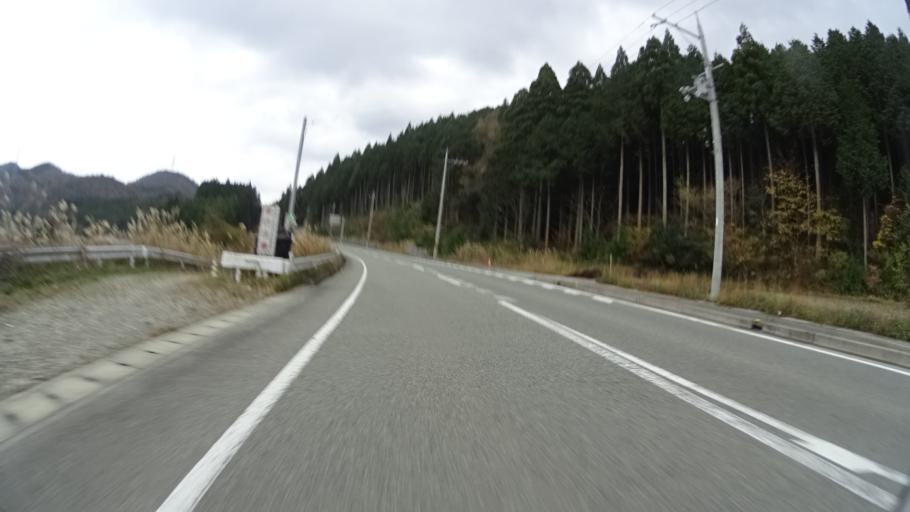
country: JP
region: Hyogo
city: Sasayama
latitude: 35.0662
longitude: 135.4033
